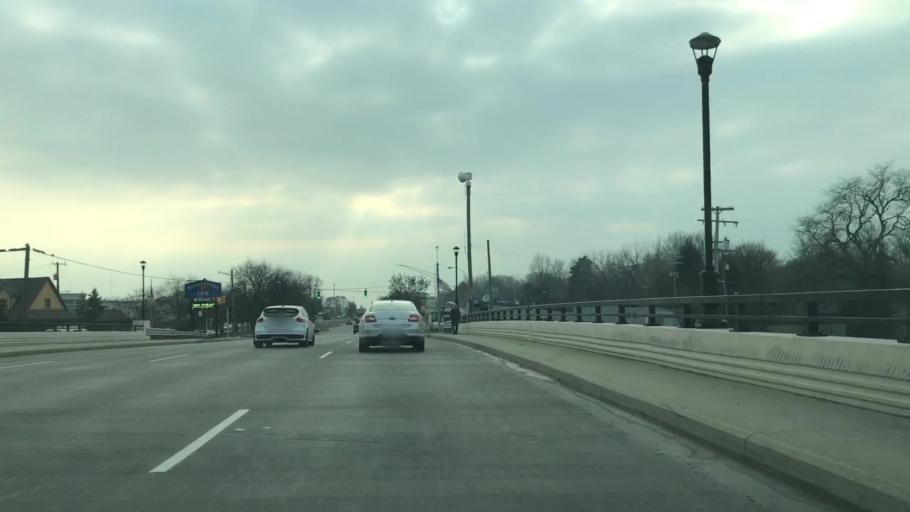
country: US
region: Michigan
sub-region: Macomb County
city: Mount Clemens
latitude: 42.5852
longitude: -82.8836
